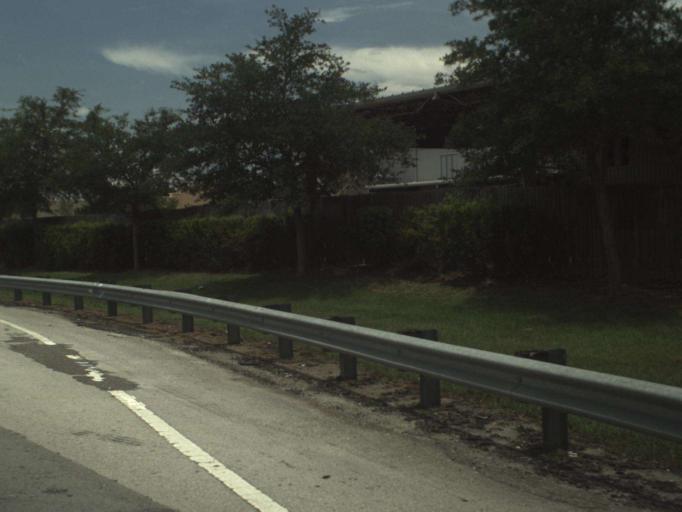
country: US
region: Florida
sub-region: Saint Lucie County
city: Lakewood Park
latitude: 27.4432
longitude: -80.3991
